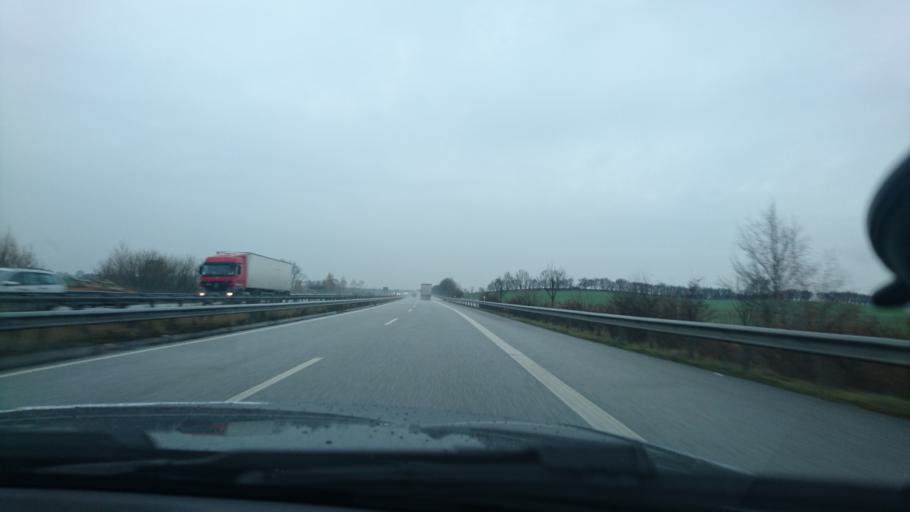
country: DE
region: Schleswig-Holstein
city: Oldenburg in Holstein
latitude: 54.3088
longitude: 10.9077
